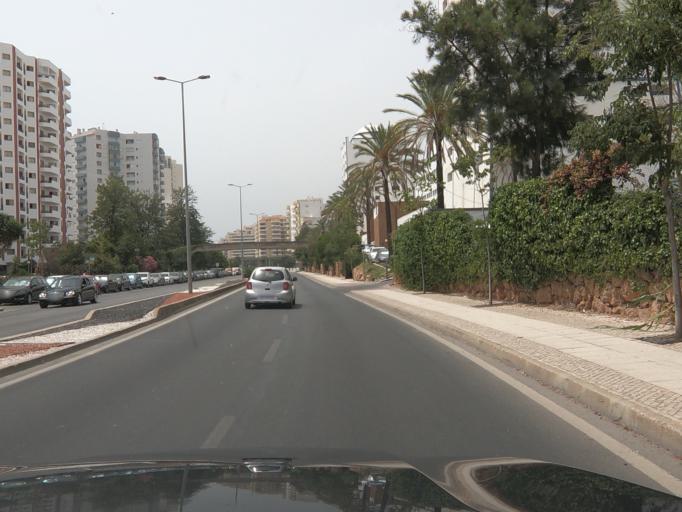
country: PT
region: Faro
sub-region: Portimao
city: Portimao
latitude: 37.1220
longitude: -8.5365
